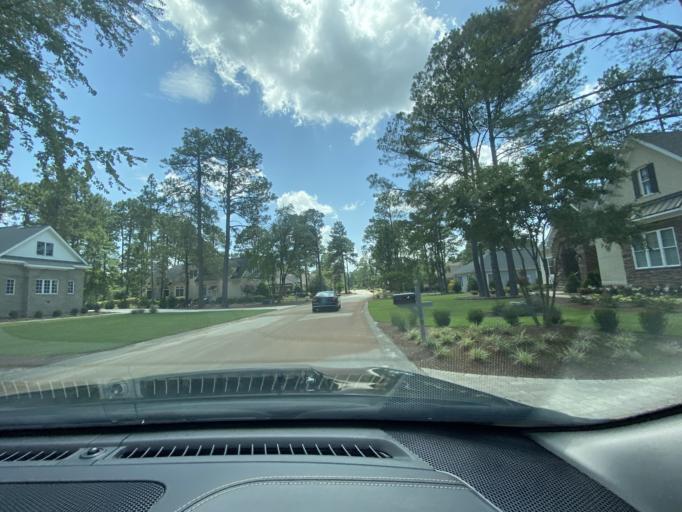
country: US
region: North Carolina
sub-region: Moore County
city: Pinehurst
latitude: 35.1921
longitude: -79.4314
